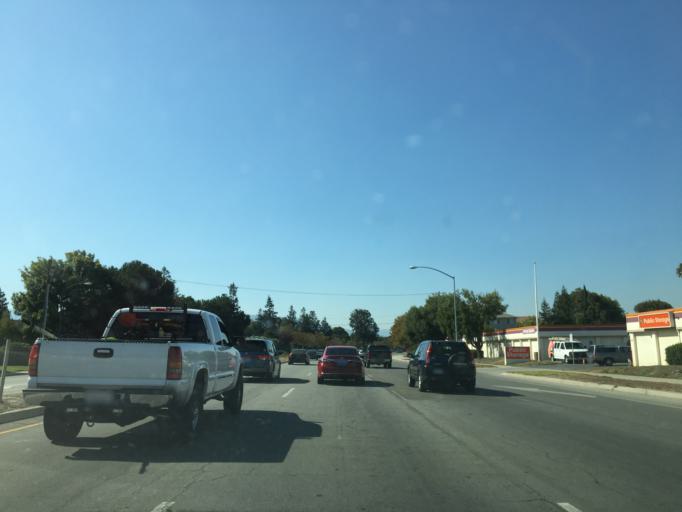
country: US
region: California
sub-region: Santa Clara County
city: Seven Trees
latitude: 37.2763
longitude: -121.8431
